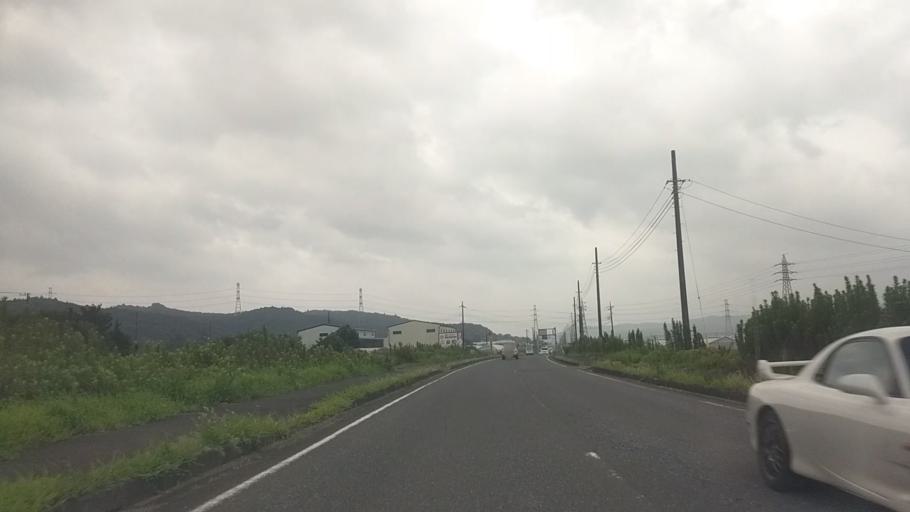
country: JP
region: Chiba
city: Kisarazu
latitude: 35.3552
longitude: 140.0547
